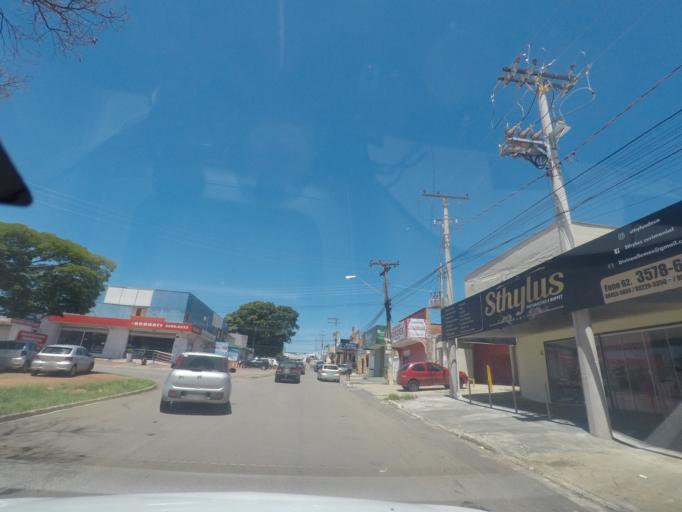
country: BR
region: Goias
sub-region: Aparecida De Goiania
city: Aparecida de Goiania
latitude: -16.7683
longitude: -49.3428
